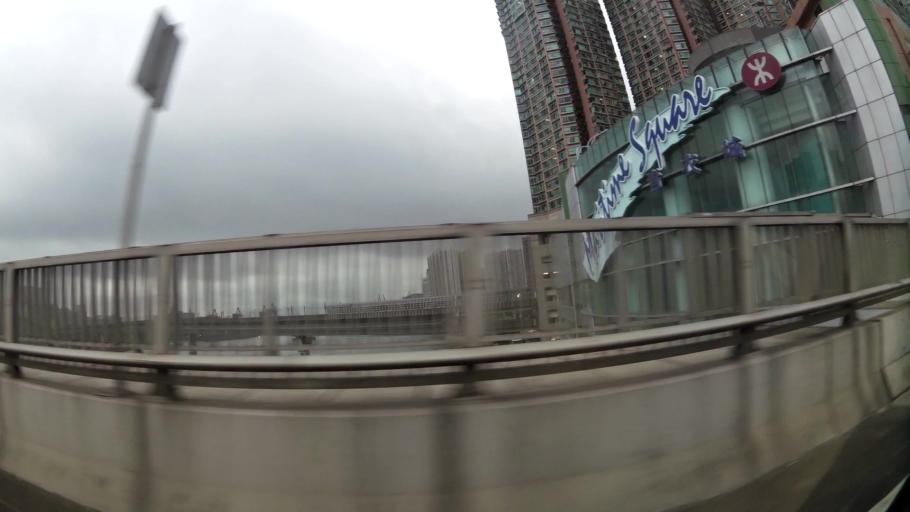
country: HK
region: Tsuen Wan
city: Tsuen Wan
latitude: 22.3597
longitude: 114.1087
